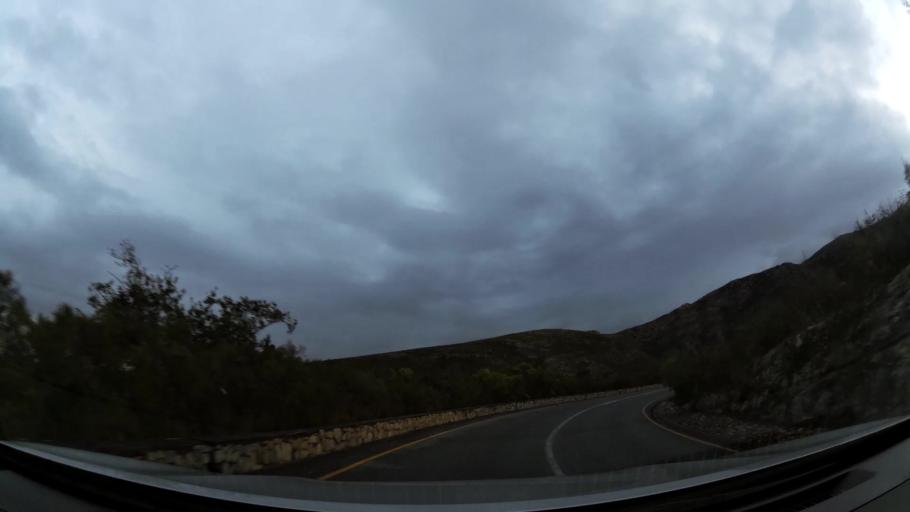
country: ZA
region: Western Cape
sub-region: Overberg District Municipality
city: Swellendam
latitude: -33.9775
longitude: 20.7073
